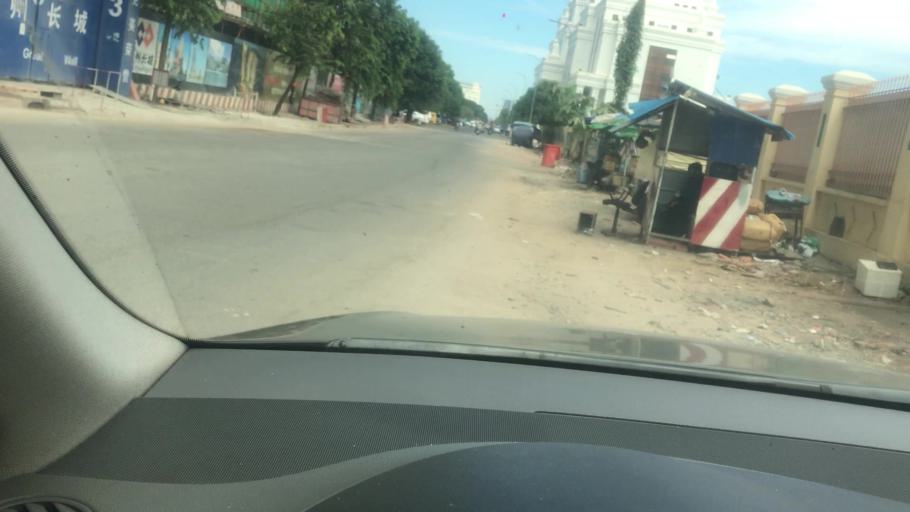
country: KH
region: Phnom Penh
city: Phnom Penh
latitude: 11.5531
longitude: 104.9386
